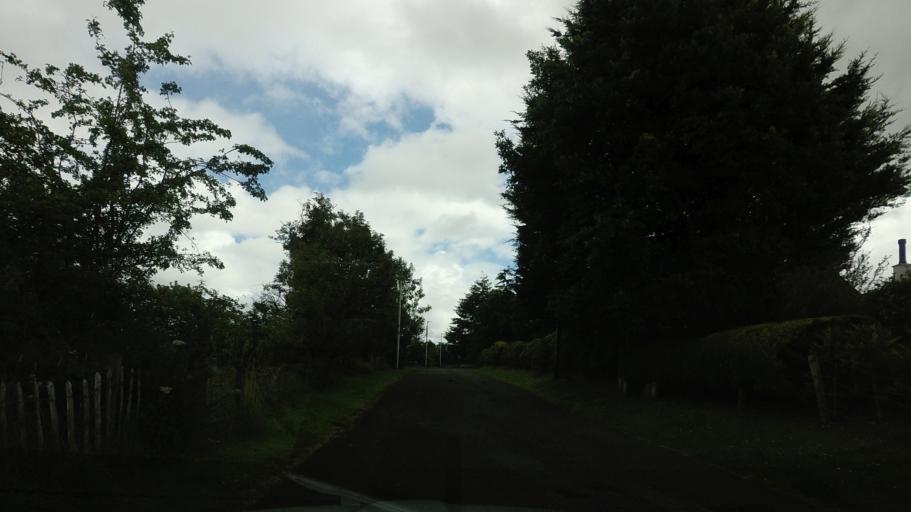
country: GB
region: Scotland
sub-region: Stirling
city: Killearn
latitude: 56.0651
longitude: -4.4475
